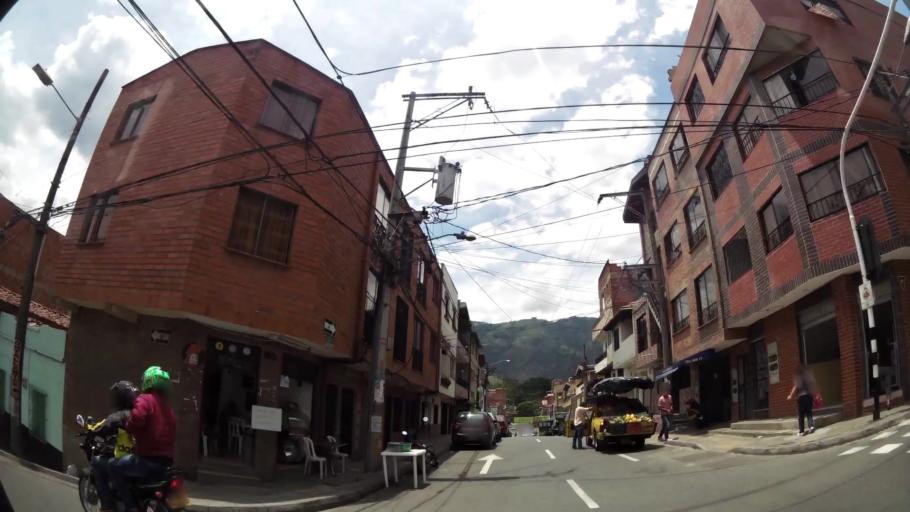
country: CO
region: Antioquia
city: Bello
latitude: 6.3330
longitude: -75.5598
